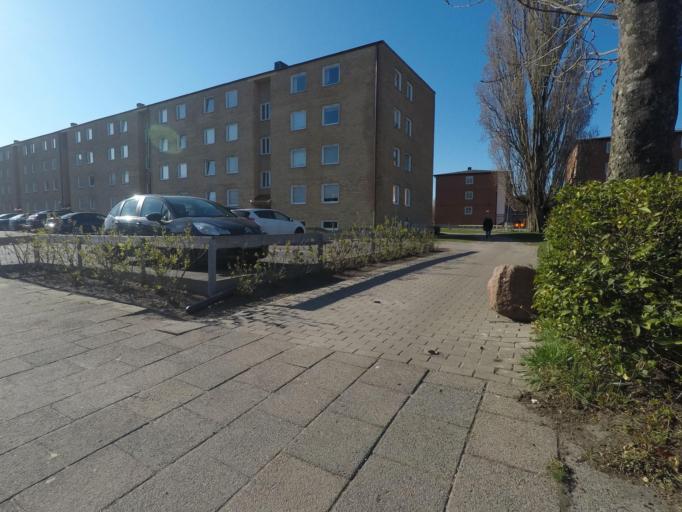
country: SE
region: Skane
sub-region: Malmo
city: Malmoe
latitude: 55.5707
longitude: 13.0188
